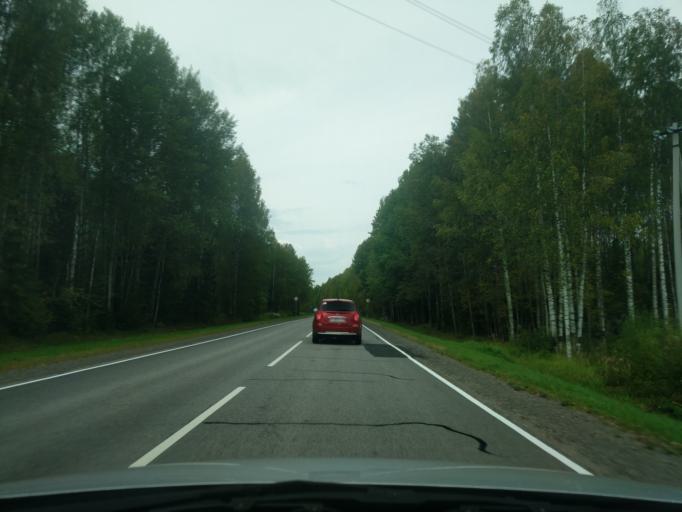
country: RU
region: Kirov
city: Kotel'nich
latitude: 58.2713
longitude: 48.0782
